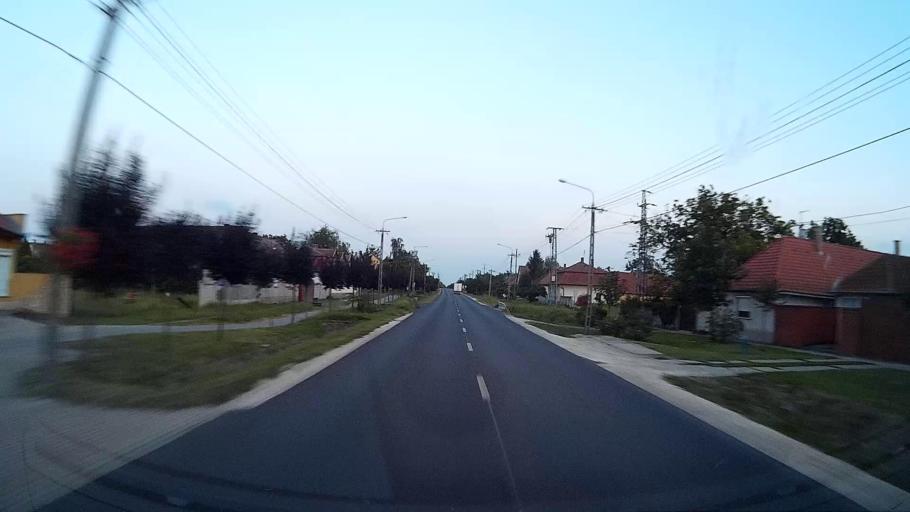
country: HU
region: Pest
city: Cegledbercel
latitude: 47.2174
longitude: 19.6731
